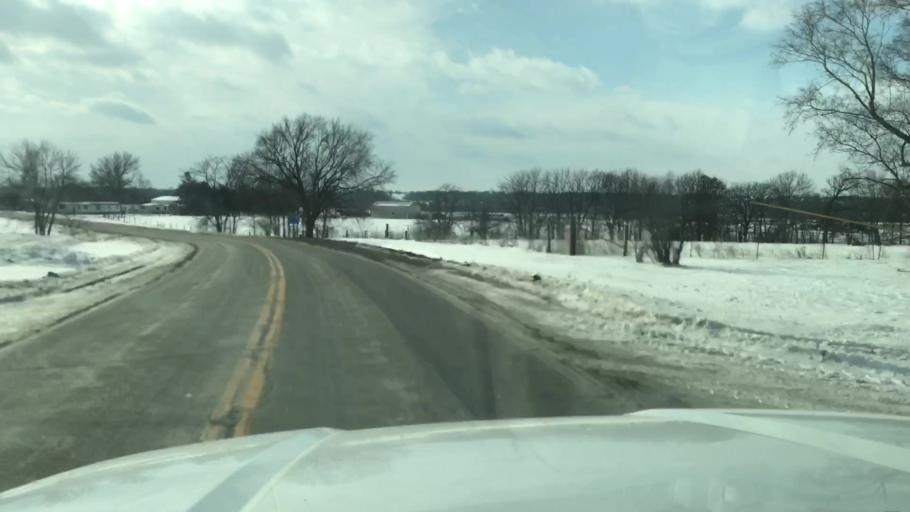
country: US
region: Missouri
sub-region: Gentry County
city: Stanberry
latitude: 40.3588
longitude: -94.6707
